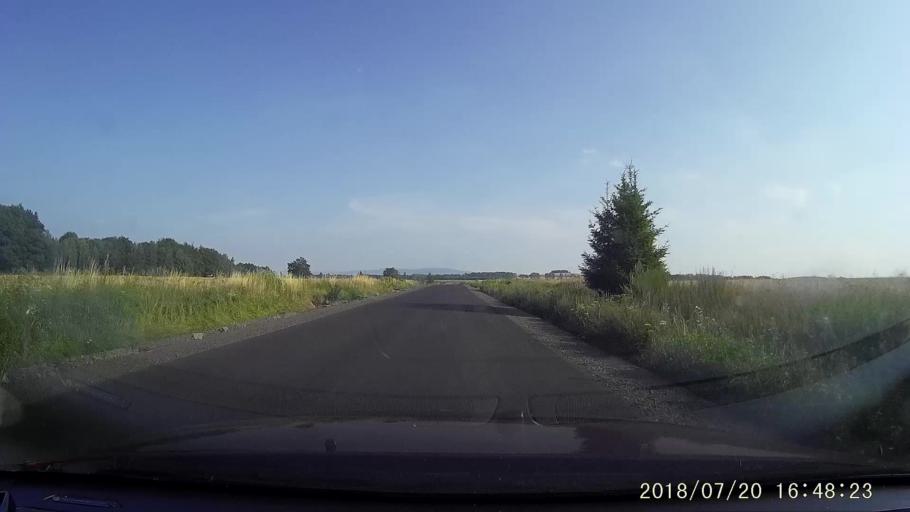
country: PL
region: Lower Silesian Voivodeship
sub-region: Powiat lubanski
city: Siekierczyn
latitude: 51.0561
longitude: 15.1878
